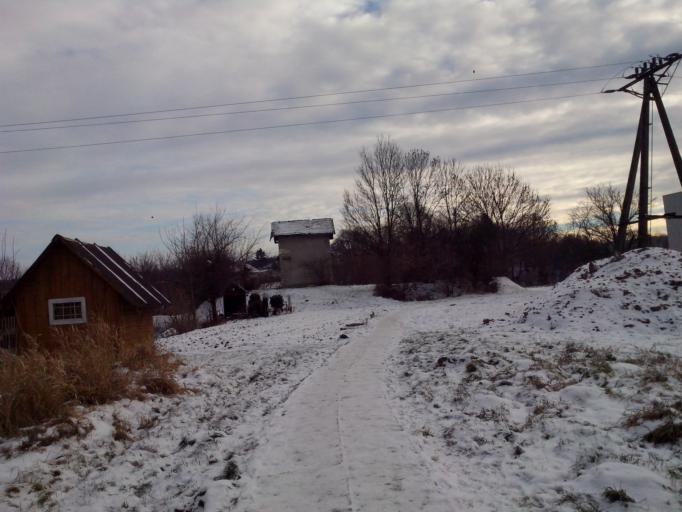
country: PL
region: Subcarpathian Voivodeship
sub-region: Powiat strzyzowski
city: Strzyzow
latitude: 49.8665
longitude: 21.8002
